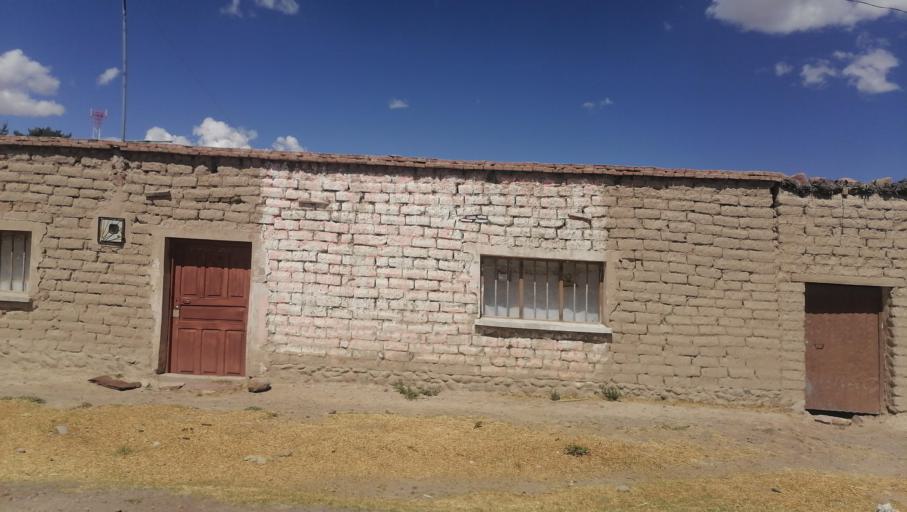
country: BO
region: Oruro
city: Challapata
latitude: -18.9075
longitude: -66.7773
